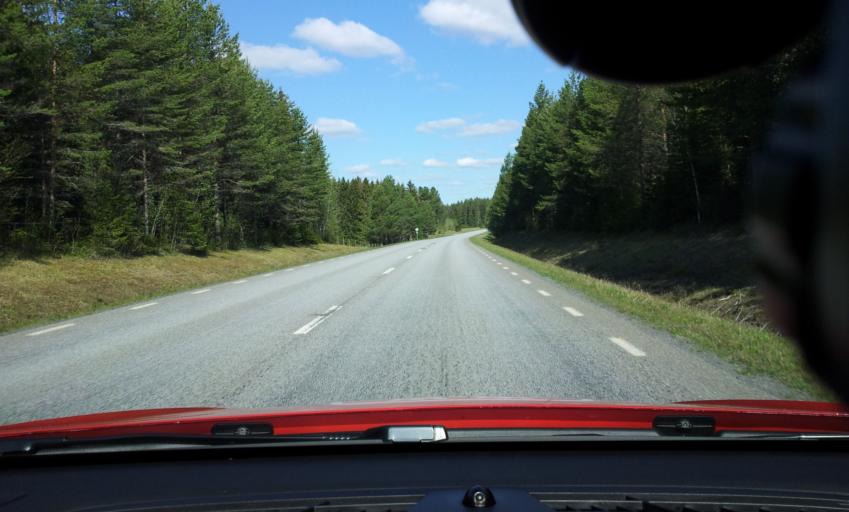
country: SE
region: Jaemtland
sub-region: Krokoms Kommun
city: Valla
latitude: 63.2731
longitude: 13.9465
